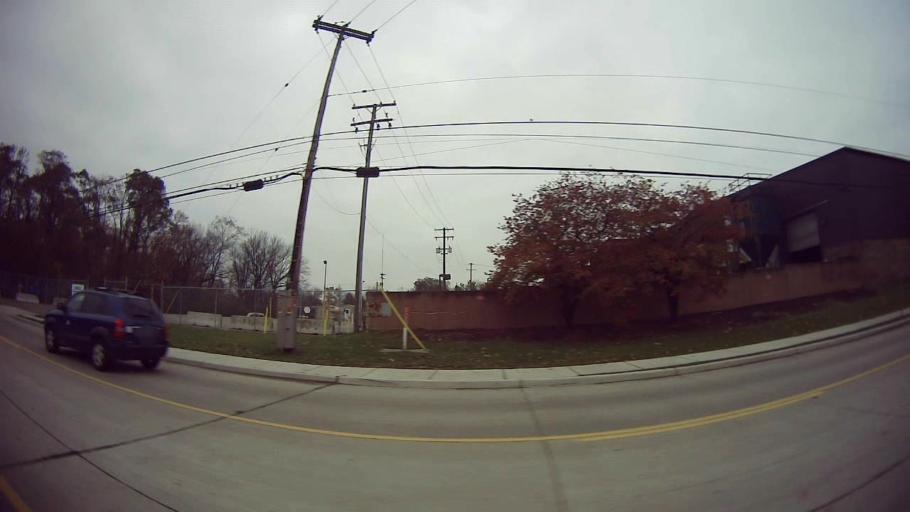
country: US
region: Michigan
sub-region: Oakland County
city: Southfield
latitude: 42.4457
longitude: -83.2395
